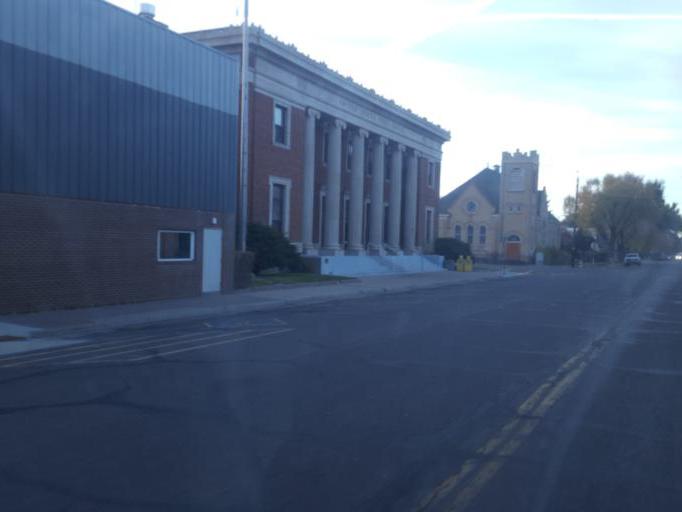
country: US
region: Colorado
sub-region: Rio Grande County
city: Monte Vista
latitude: 37.5799
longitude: -106.1481
